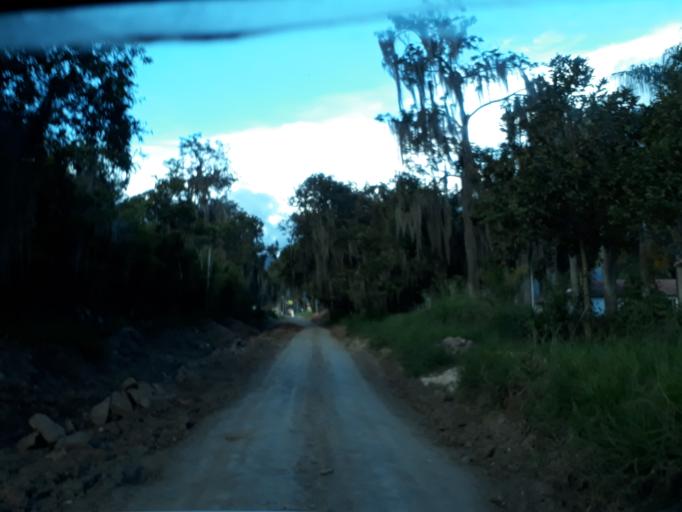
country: CO
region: Cundinamarca
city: Pacho
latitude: 5.1506
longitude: -74.1550
